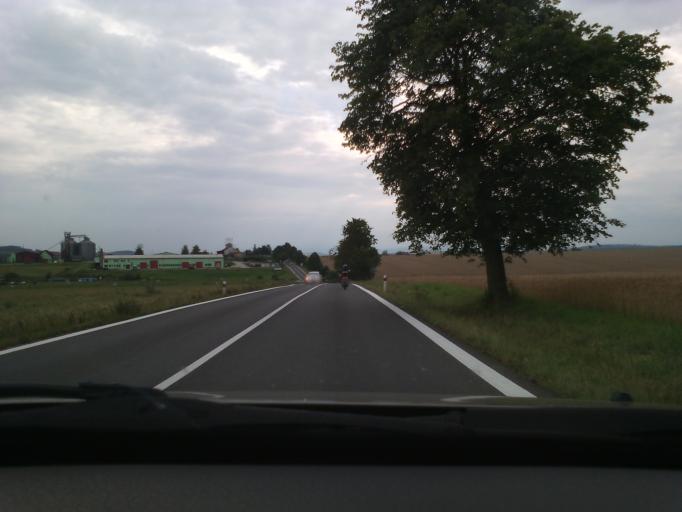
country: SK
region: Presovsky
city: Spisska Bela
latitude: 49.1981
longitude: 20.4669
